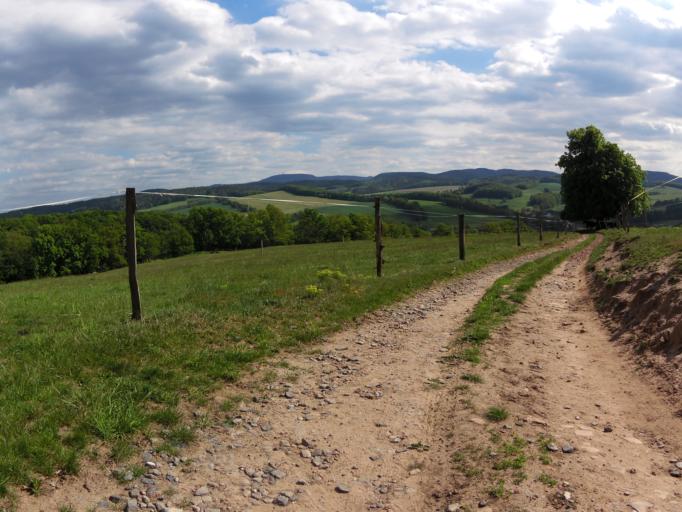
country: DE
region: Thuringia
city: Seebach
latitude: 50.9518
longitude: 10.4320
